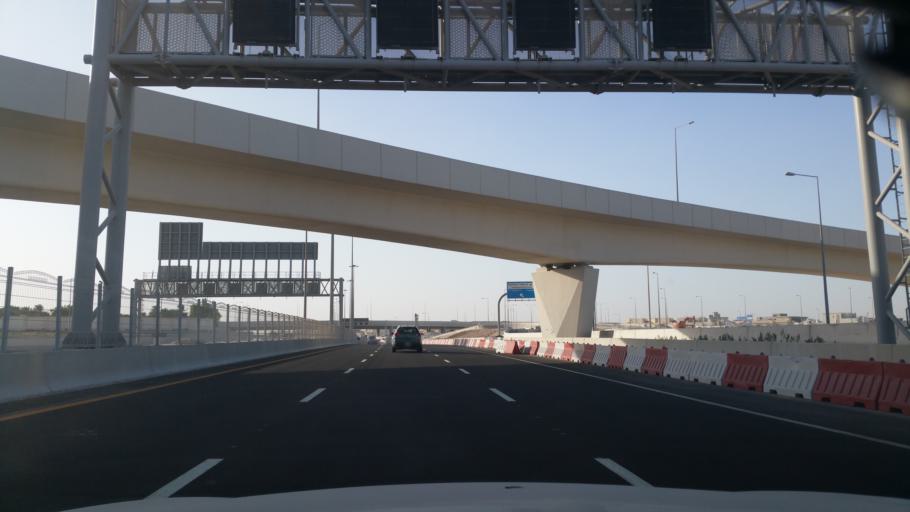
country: QA
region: Baladiyat ad Dawhah
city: Doha
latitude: 25.2342
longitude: 51.5271
